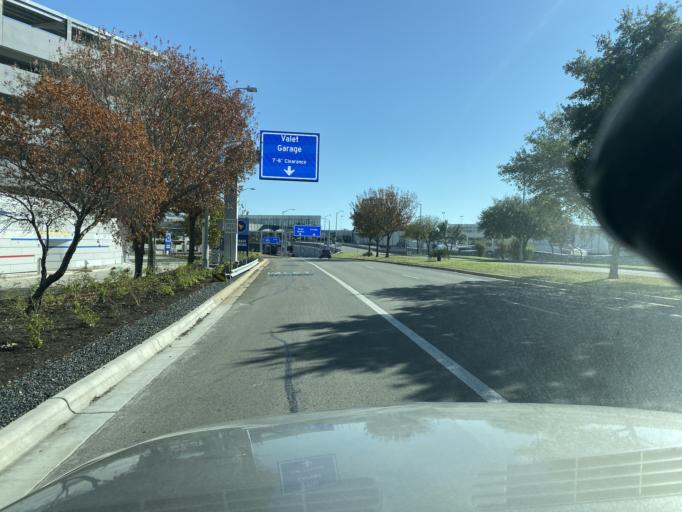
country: US
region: Texas
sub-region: Travis County
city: Austin
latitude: 30.2047
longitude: -97.6705
